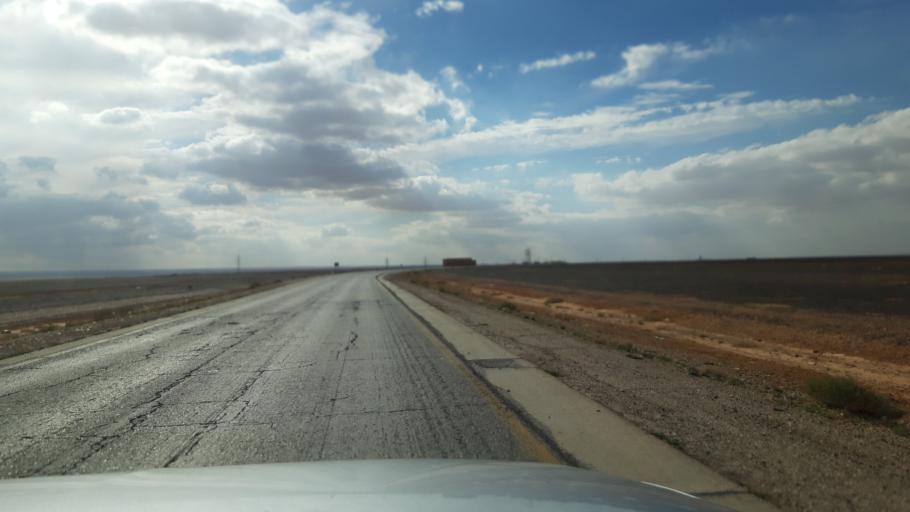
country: JO
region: Amman
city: Al Azraq ash Shamali
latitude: 31.7287
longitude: 36.4716
